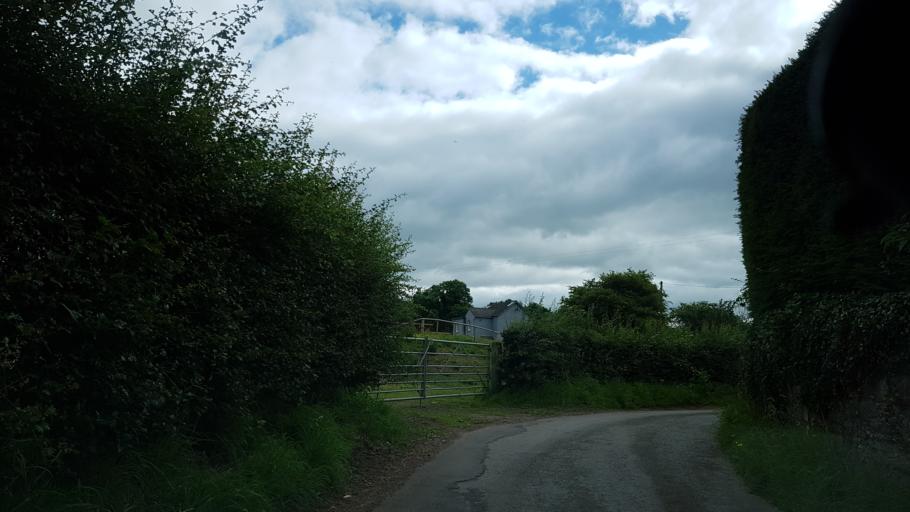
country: GB
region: Wales
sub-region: Monmouthshire
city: Abergavenny
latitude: 51.7958
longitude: -3.0014
